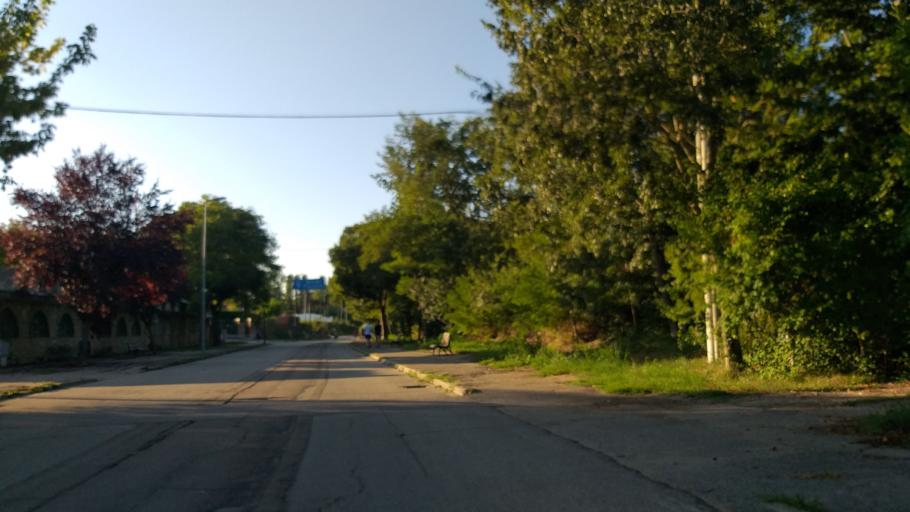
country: IT
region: Piedmont
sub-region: Provincia di Asti
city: Asti
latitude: 44.9184
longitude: 8.2016
